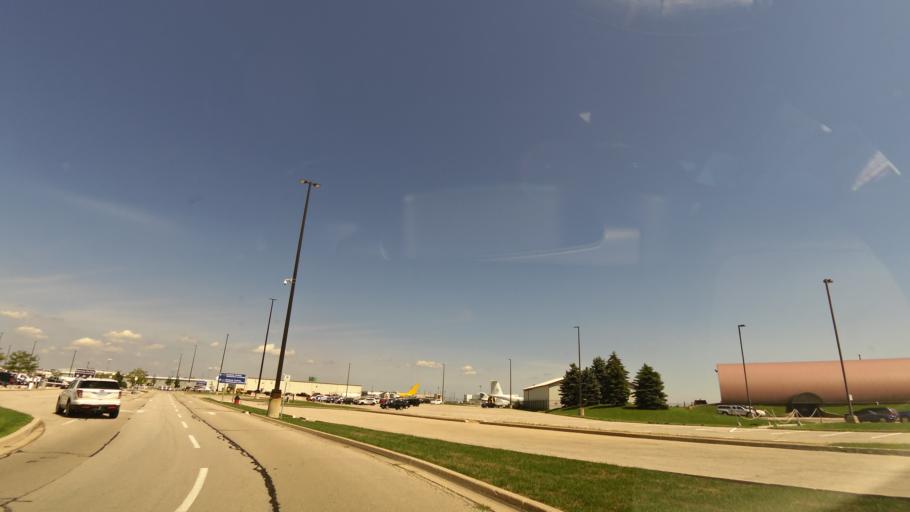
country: CA
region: Ontario
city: Ancaster
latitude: 43.1600
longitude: -79.9270
